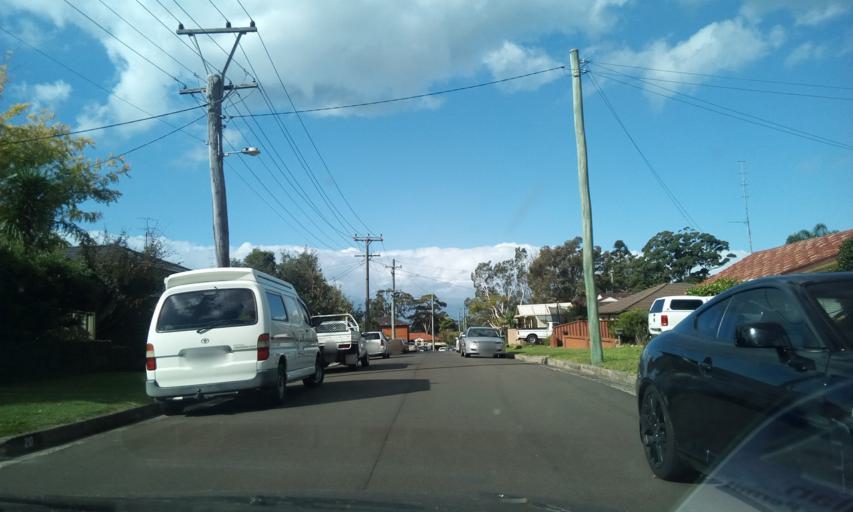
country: AU
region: New South Wales
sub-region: Wollongong
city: Keiraville
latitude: -34.4118
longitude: 150.8686
